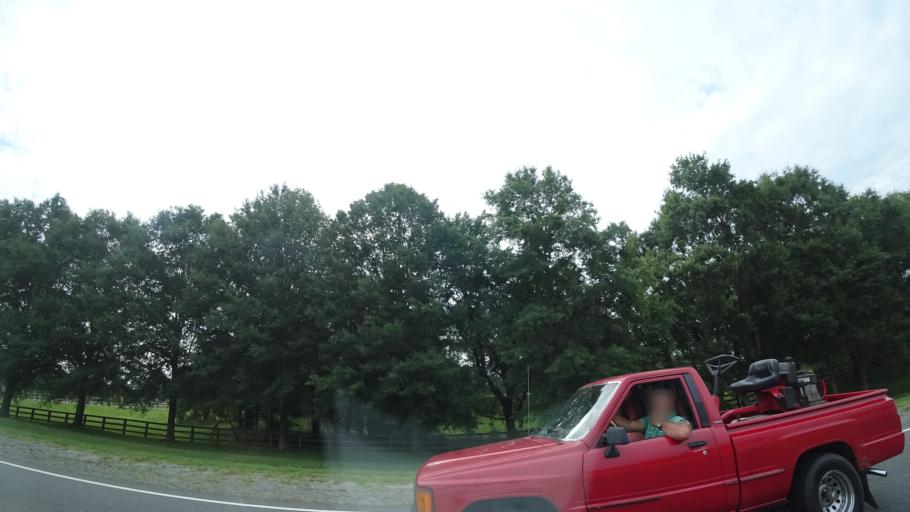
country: US
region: Virginia
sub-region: Spotsylvania County
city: Spotsylvania
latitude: 38.2207
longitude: -77.5681
